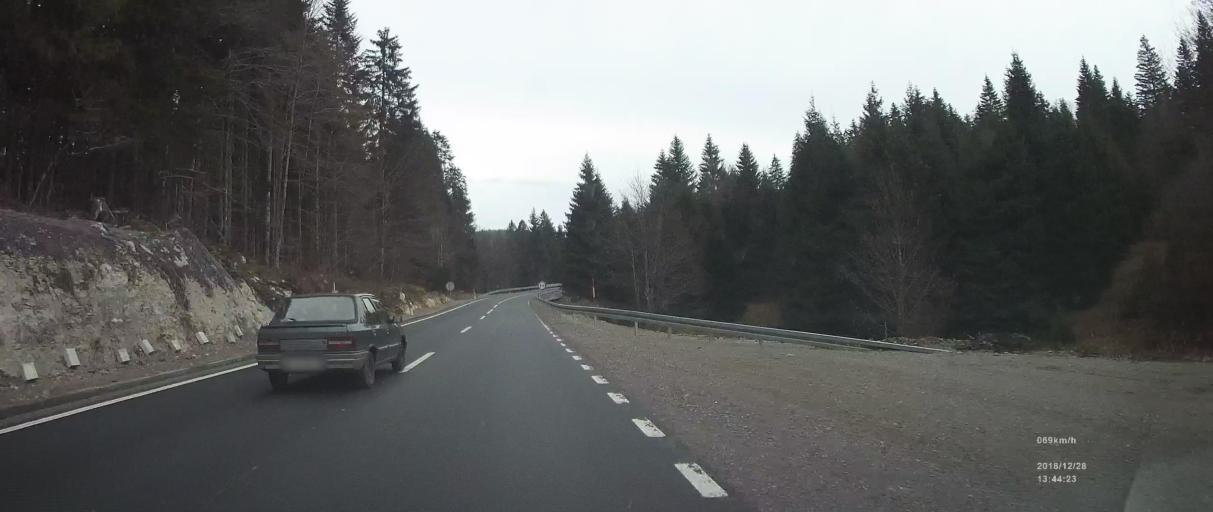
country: HR
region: Primorsko-Goranska
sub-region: Grad Delnice
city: Delnice
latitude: 45.3731
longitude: 14.7825
